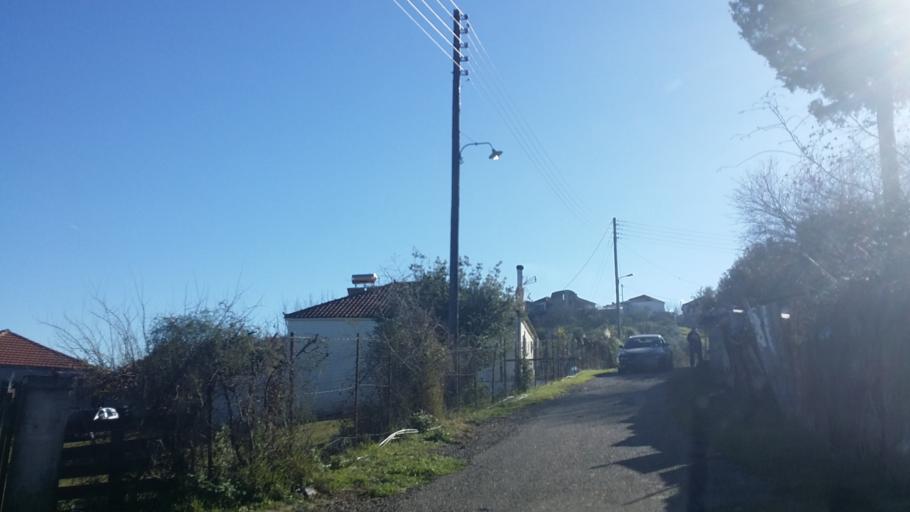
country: GR
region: West Greece
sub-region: Nomos Aitolias kai Akarnanias
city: Fitiai
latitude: 38.7135
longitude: 21.1734
